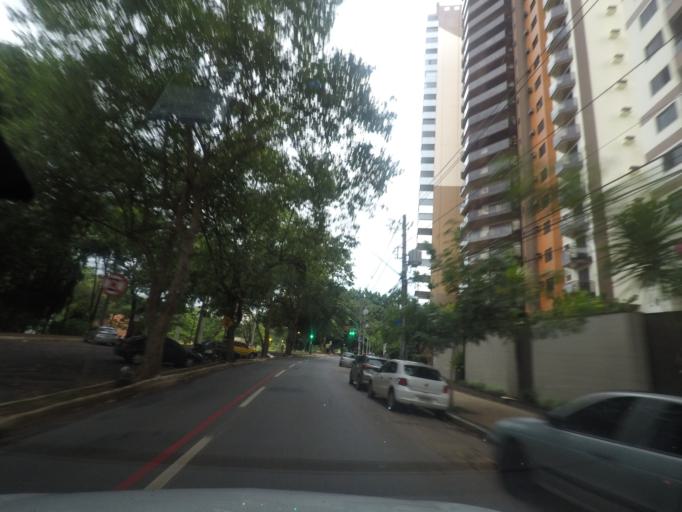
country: BR
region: Goias
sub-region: Goiania
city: Goiania
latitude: -16.6814
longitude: -49.2713
